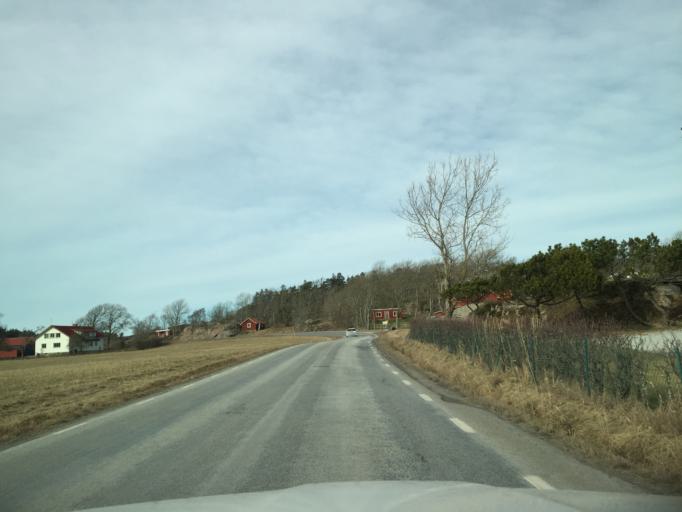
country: SE
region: Vaestra Goetaland
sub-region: Tjorns Kommun
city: Skaerhamn
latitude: 58.0232
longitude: 11.6122
